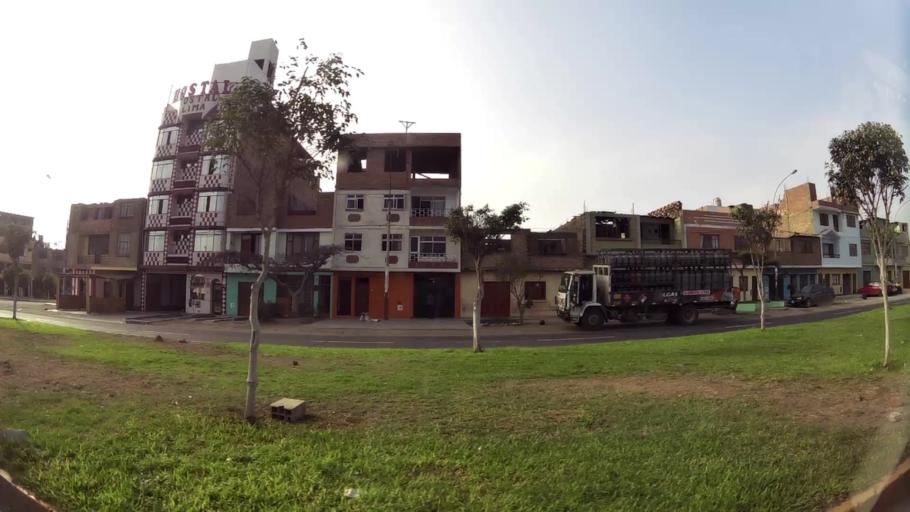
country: PE
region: Callao
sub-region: Callao
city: Callao
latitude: -12.0291
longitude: -77.0825
